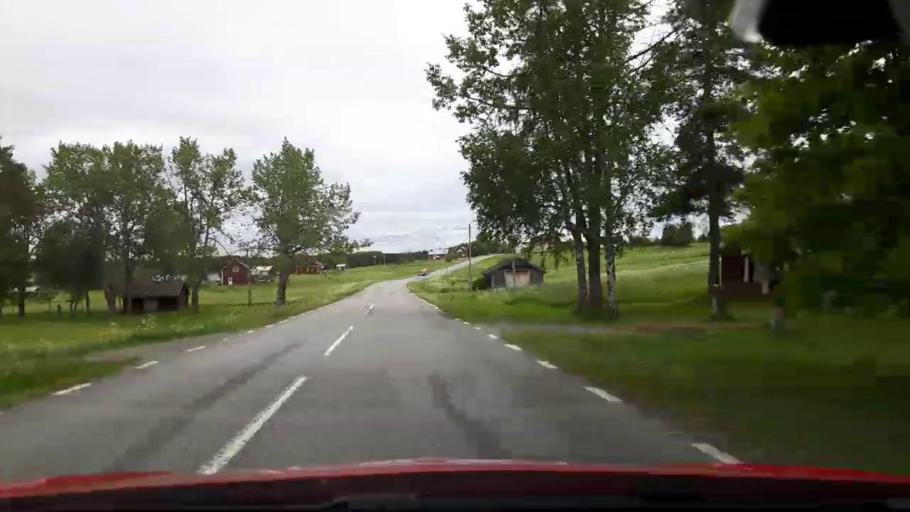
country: SE
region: Jaemtland
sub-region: Stroemsunds Kommun
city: Stroemsund
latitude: 63.5597
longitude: 15.3998
